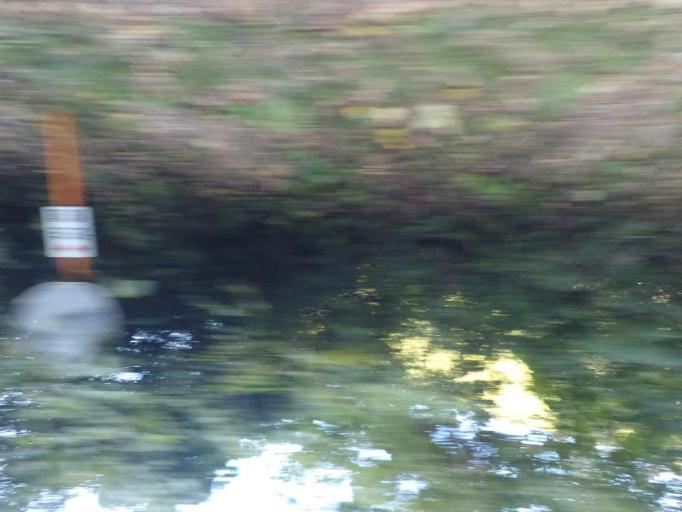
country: JP
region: Nagano
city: Shiojiri
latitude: 36.0049
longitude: 137.7707
